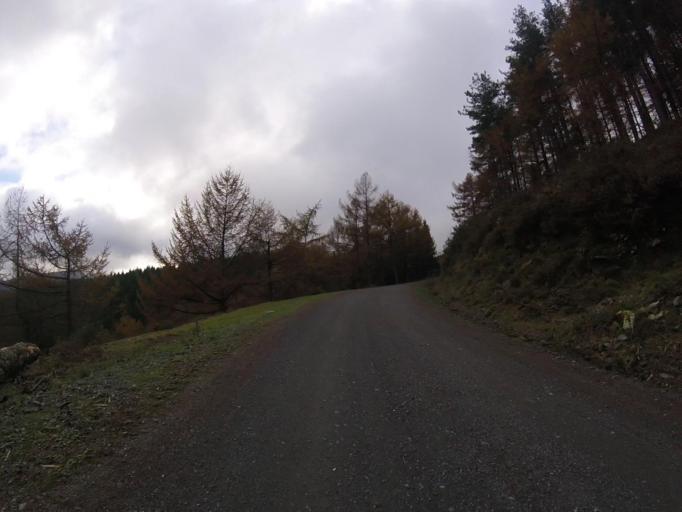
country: ES
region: Navarre
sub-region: Provincia de Navarra
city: Goizueta
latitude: 43.2109
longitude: -1.8241
